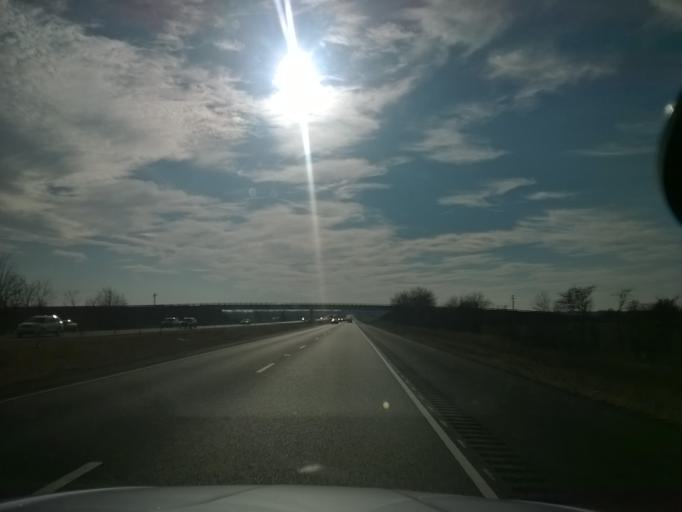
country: US
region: Indiana
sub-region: Johnson County
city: Edinburgh
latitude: 39.3197
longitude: -85.9469
